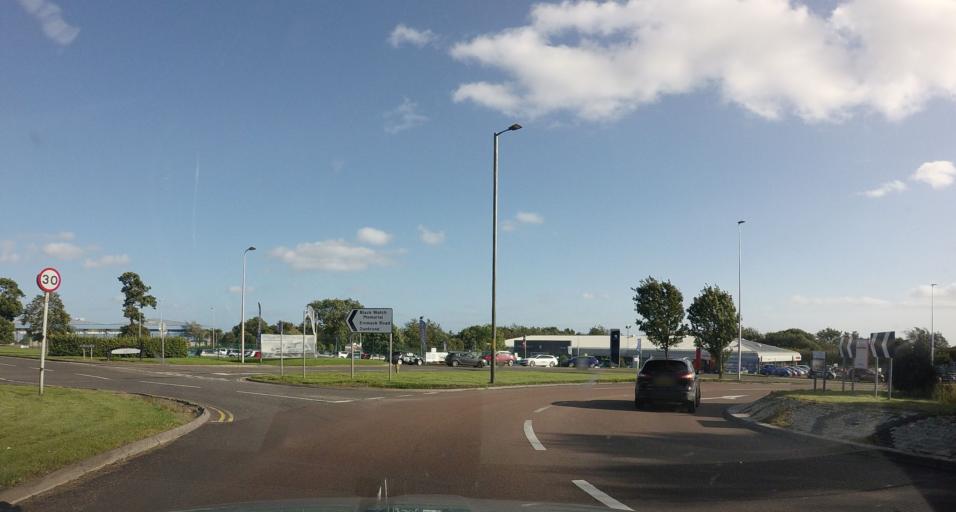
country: GB
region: Scotland
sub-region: Dundee City
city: Dundee
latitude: 56.4949
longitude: -2.9497
